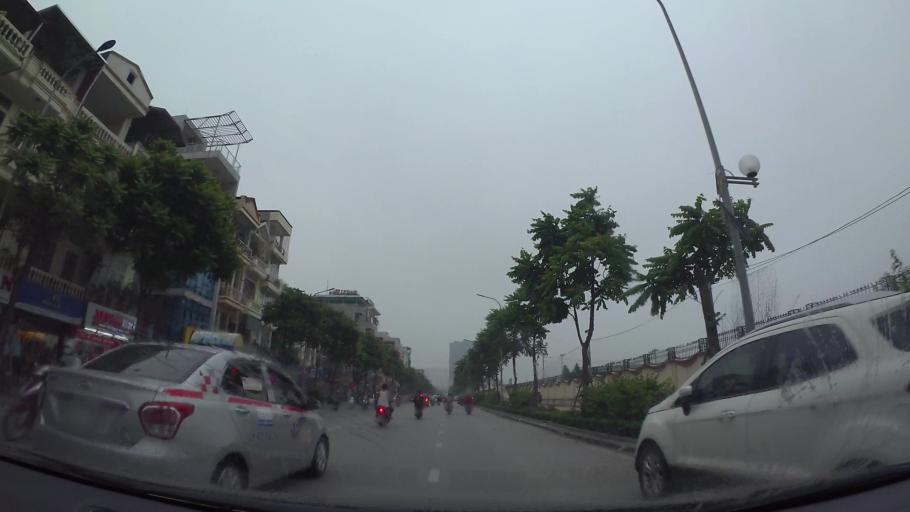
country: VN
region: Ha Noi
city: Hai BaTrung
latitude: 20.9933
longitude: 105.8318
